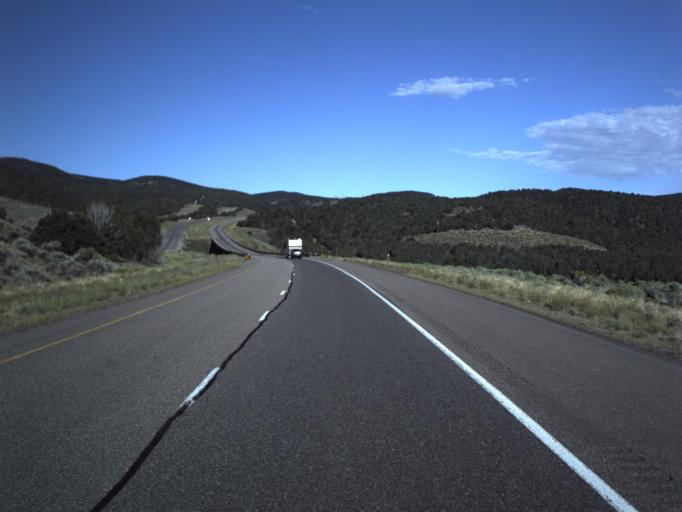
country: US
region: Utah
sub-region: Sevier County
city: Monroe
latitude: 38.5727
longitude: -112.4554
